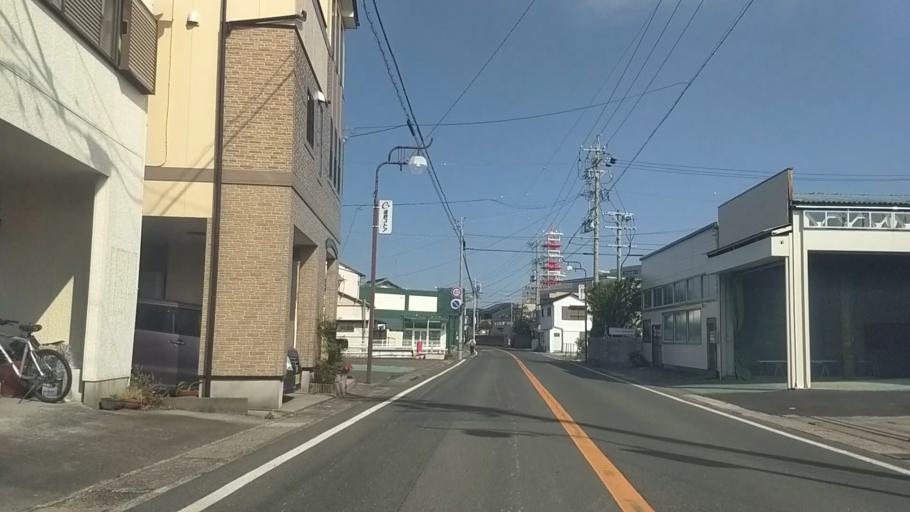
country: JP
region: Shizuoka
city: Hamamatsu
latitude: 34.7034
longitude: 137.7540
